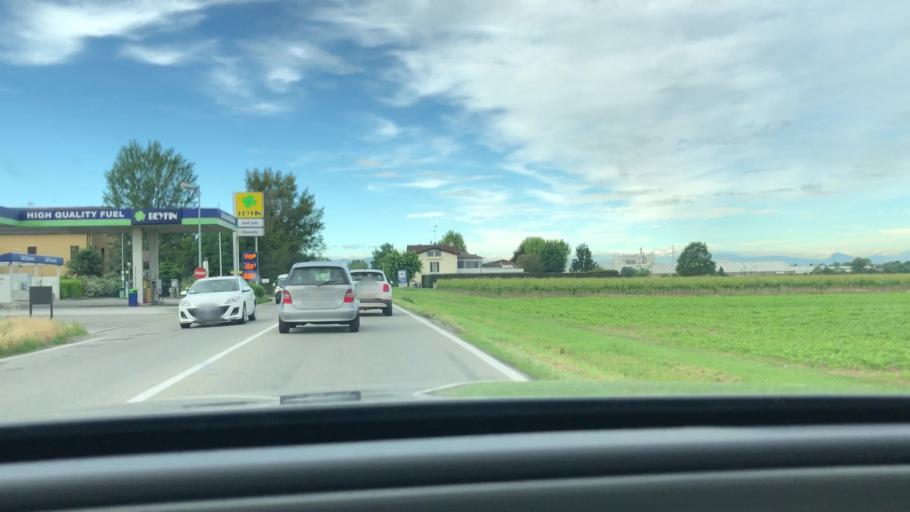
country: IT
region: Emilia-Romagna
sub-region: Provincia di Modena
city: San Damaso
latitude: 44.6068
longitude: 10.9342
